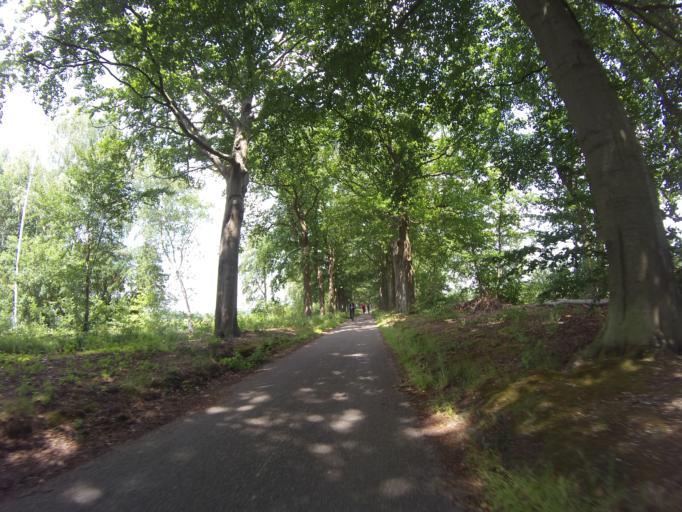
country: NL
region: Utrecht
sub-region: Gemeente De Bilt
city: De Bilt
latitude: 52.1325
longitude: 5.1604
